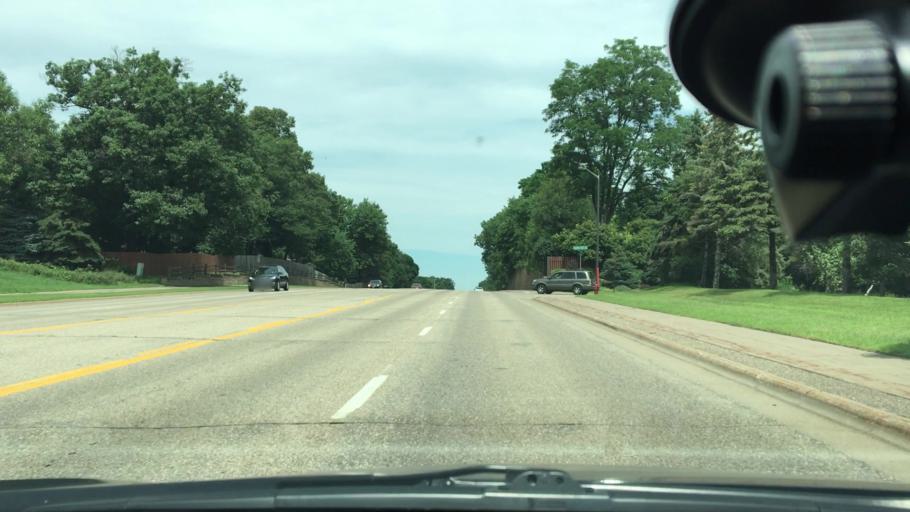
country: US
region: Minnesota
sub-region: Hennepin County
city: Maple Grove
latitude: 45.0687
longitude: -93.4309
